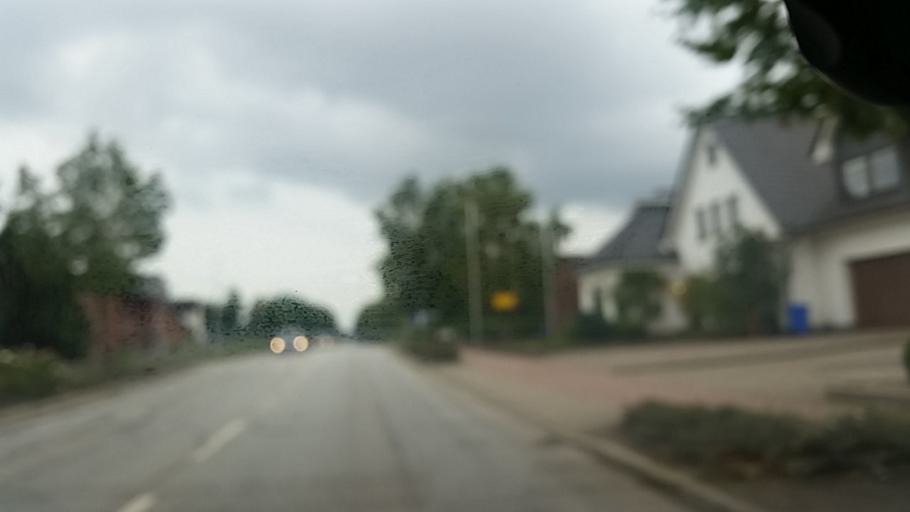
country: DE
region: Schleswig-Holstein
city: Leezen
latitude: 53.8641
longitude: 10.2506
